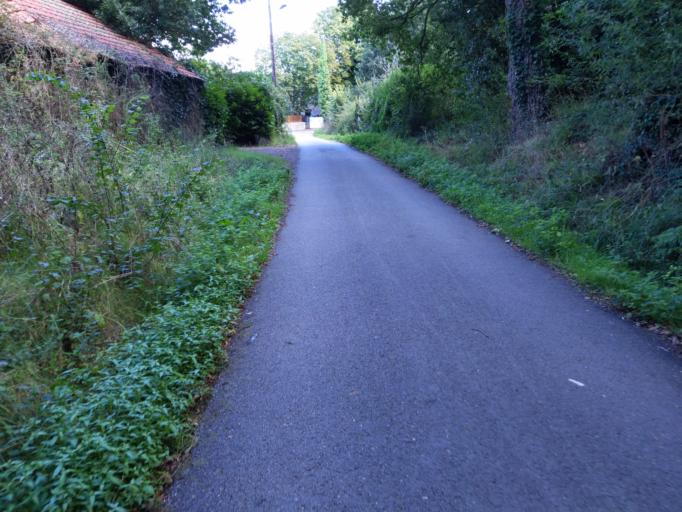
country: FR
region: Pays de la Loire
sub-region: Departement de la Loire-Atlantique
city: Saint-Nazaire
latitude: 47.2771
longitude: -2.2605
